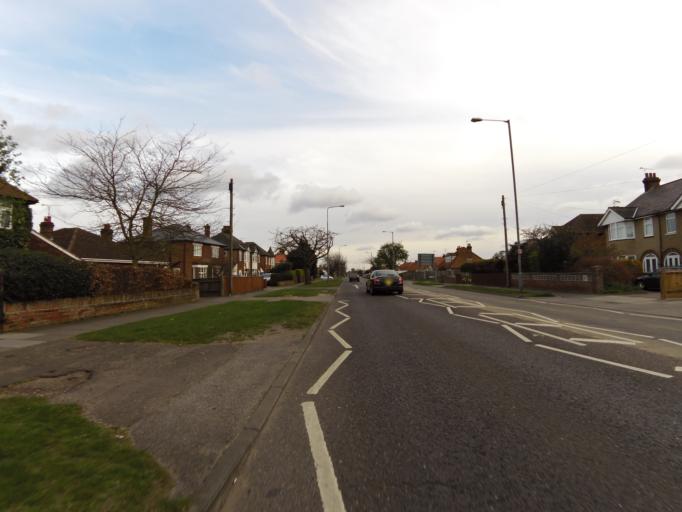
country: GB
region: England
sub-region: Suffolk
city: Kesgrave
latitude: 52.0500
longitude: 1.2011
